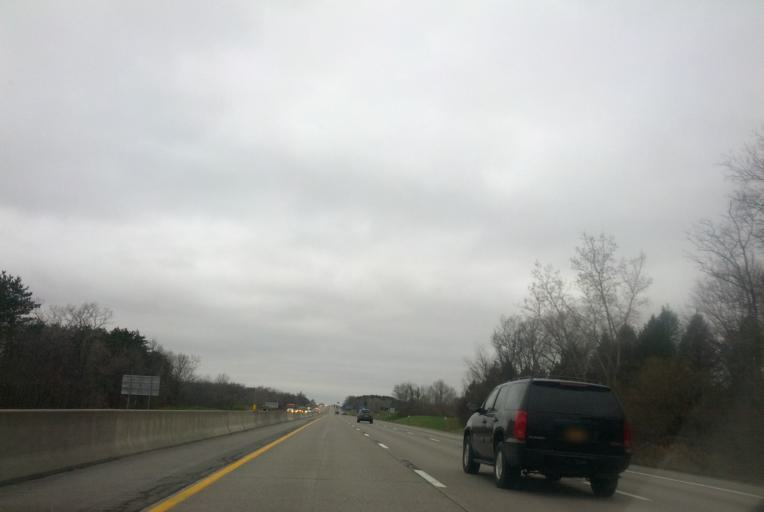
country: US
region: New York
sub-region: Ontario County
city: Victor
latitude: 42.9967
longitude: -77.3850
